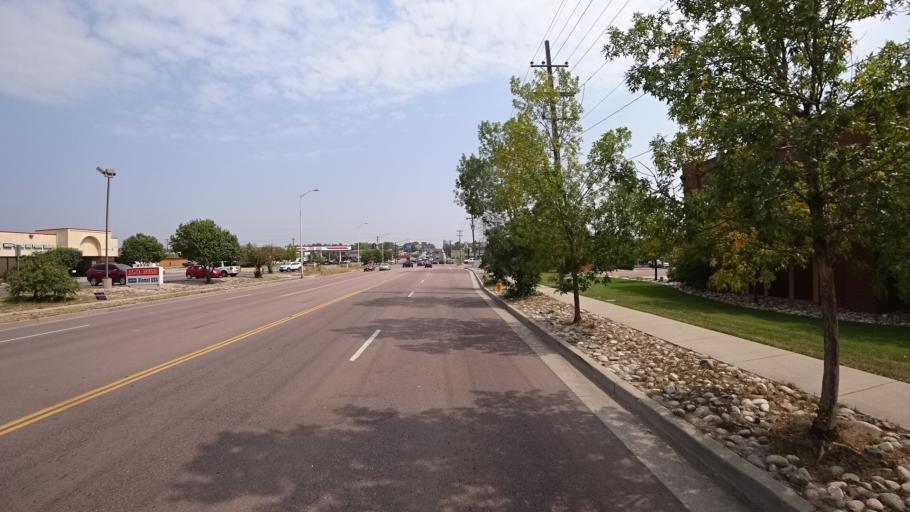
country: US
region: Colorado
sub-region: El Paso County
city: Stratmoor
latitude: 38.8254
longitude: -104.7598
